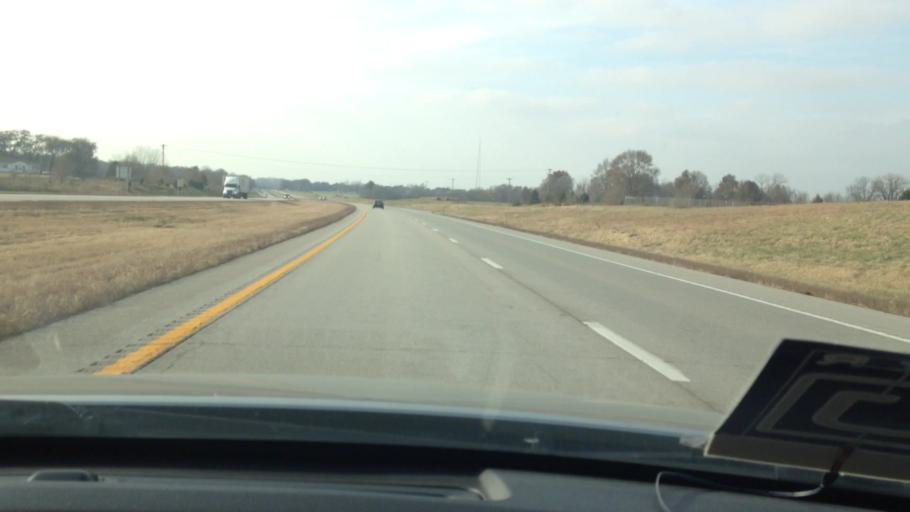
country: US
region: Missouri
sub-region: Cass County
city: Garden City
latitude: 38.5016
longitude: -94.0727
